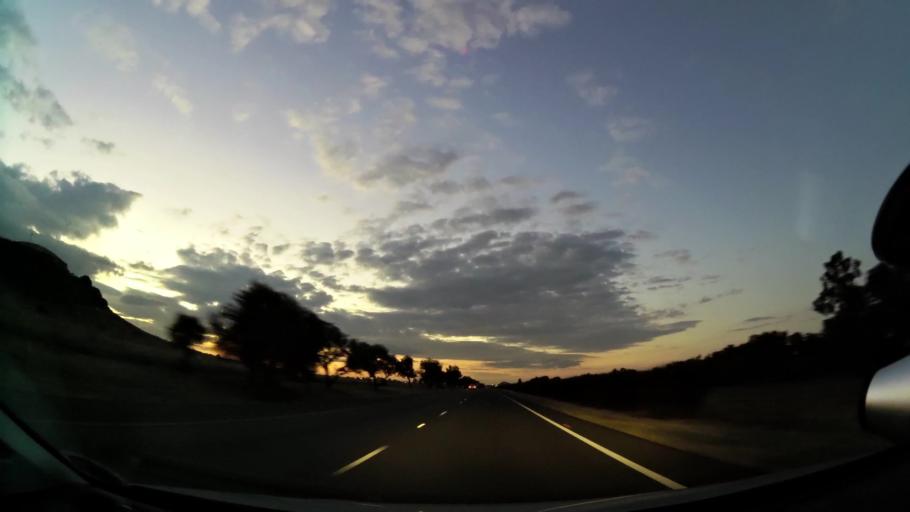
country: ZA
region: Orange Free State
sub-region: Mangaung Metropolitan Municipality
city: Bloemfontein
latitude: -29.1435
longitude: 26.1703
